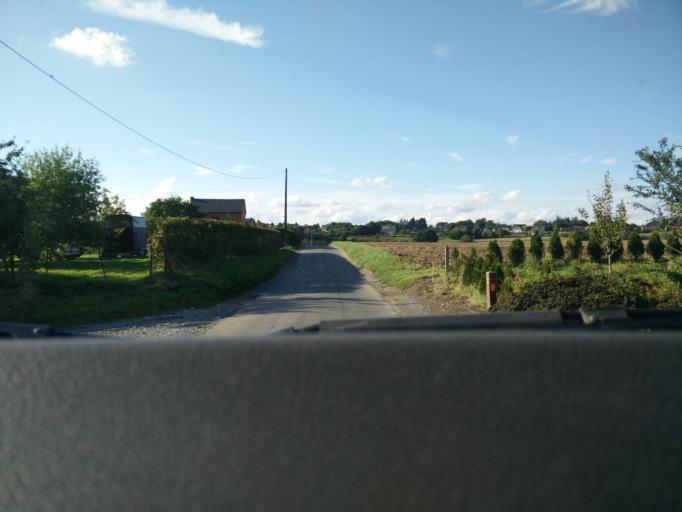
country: BE
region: Wallonia
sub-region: Province du Hainaut
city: Beaumont
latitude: 50.2299
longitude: 4.2474
